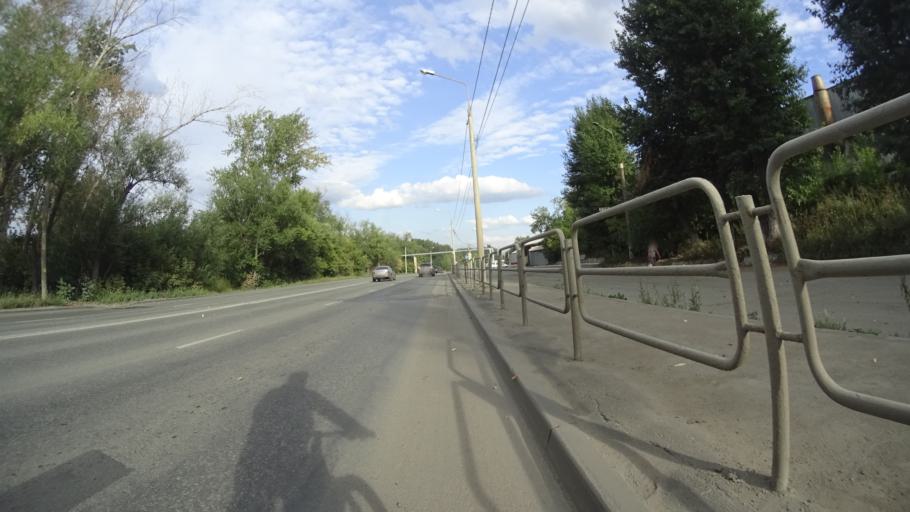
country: RU
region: Chelyabinsk
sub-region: Gorod Chelyabinsk
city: Chelyabinsk
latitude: 55.1958
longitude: 61.3802
